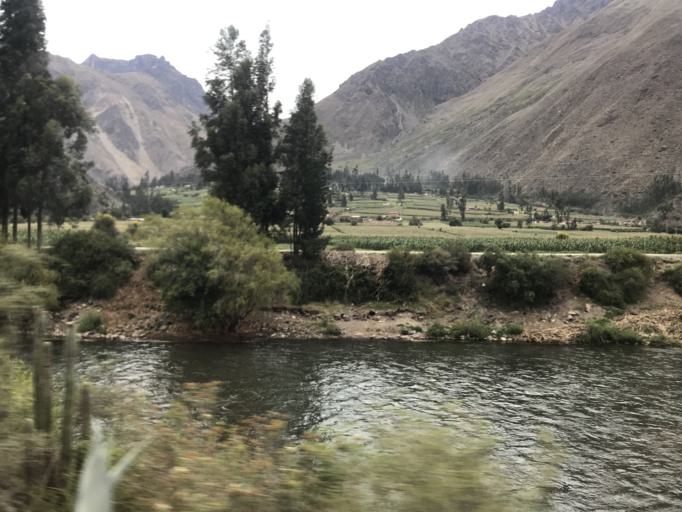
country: PE
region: Cusco
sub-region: Provincia de Urubamba
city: Ollantaytambo
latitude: -13.2241
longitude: -72.3306
